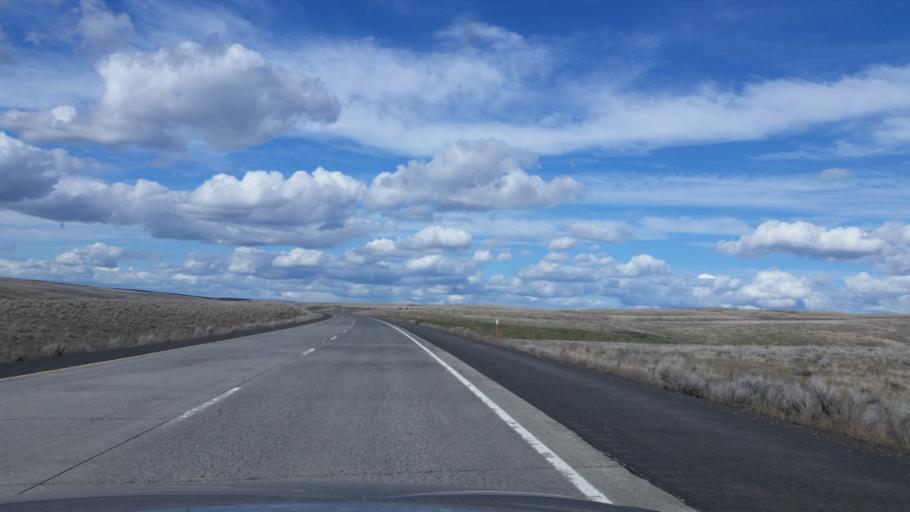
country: US
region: Washington
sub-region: Adams County
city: Ritzville
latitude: 46.8911
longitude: -118.6137
